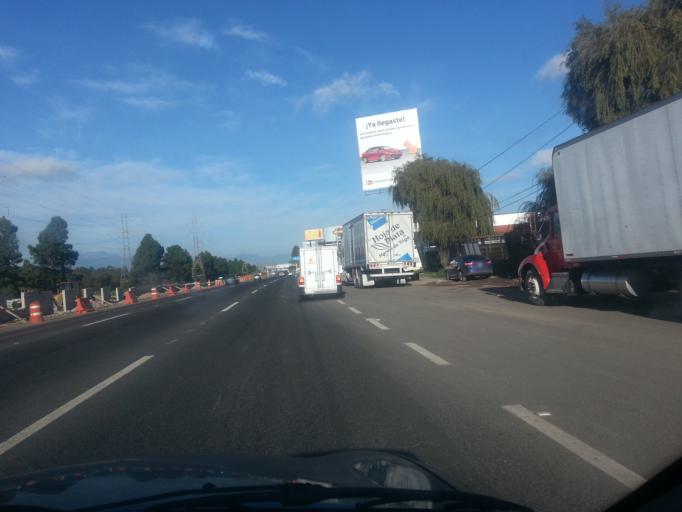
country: MX
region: Morelos
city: Ocoyoacac
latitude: 19.2876
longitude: -99.4443
